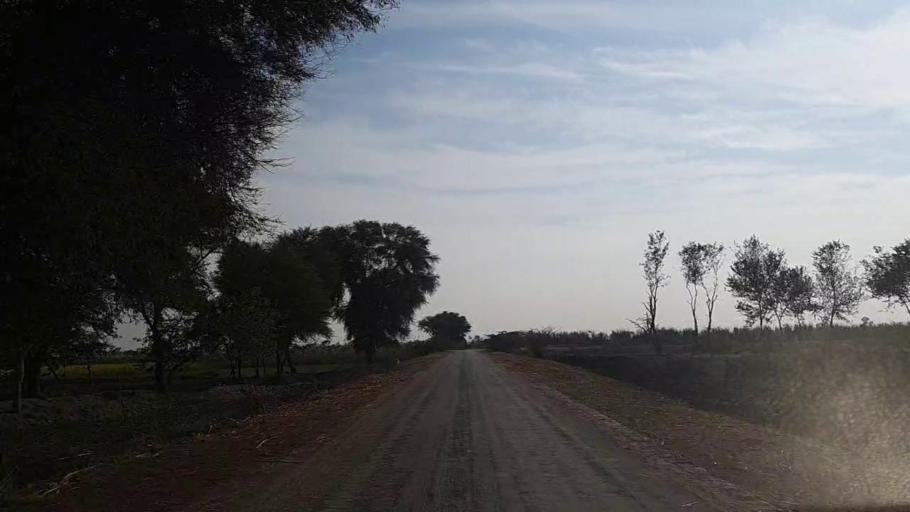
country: PK
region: Sindh
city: Daur
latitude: 26.4626
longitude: 68.4175
